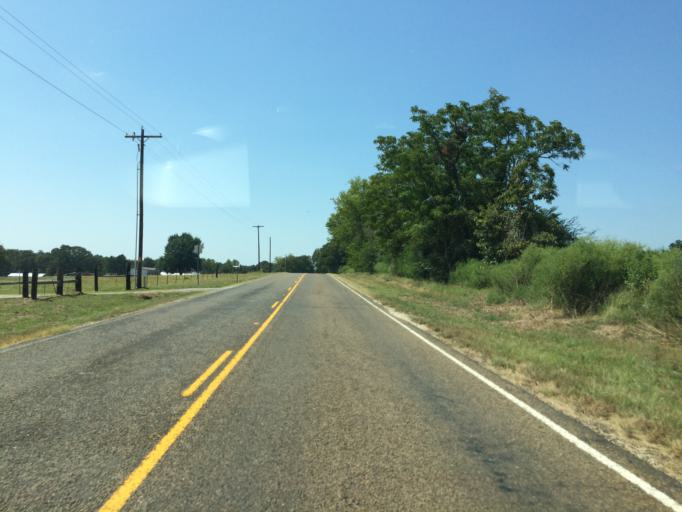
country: US
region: Texas
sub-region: Wood County
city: Quitman
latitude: 32.7174
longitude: -95.3788
